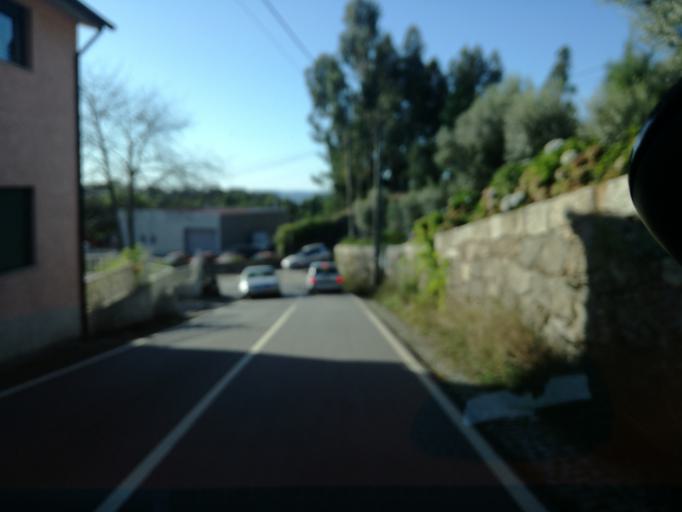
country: PT
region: Porto
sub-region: Santo Tirso
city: Sao Miguel do Couto
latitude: 41.3050
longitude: -8.4533
